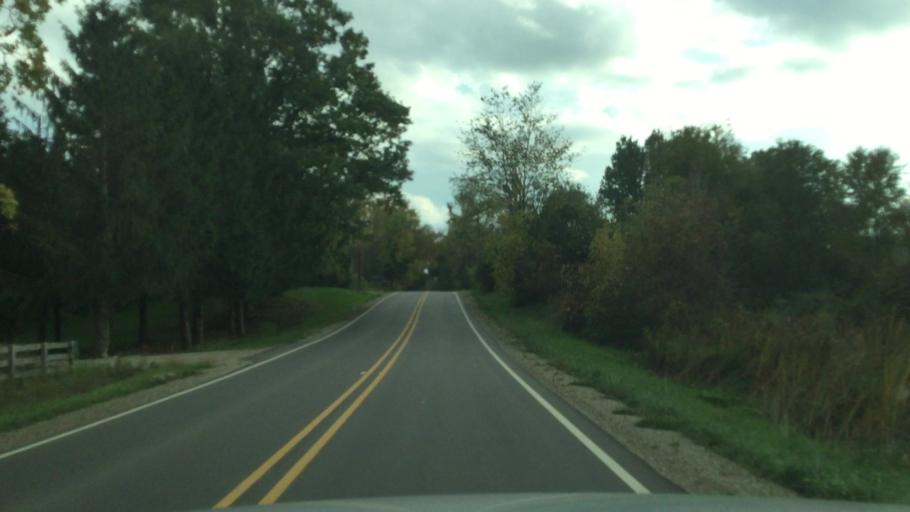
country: US
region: Michigan
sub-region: Genesee County
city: Fenton
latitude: 42.7034
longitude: -83.7031
